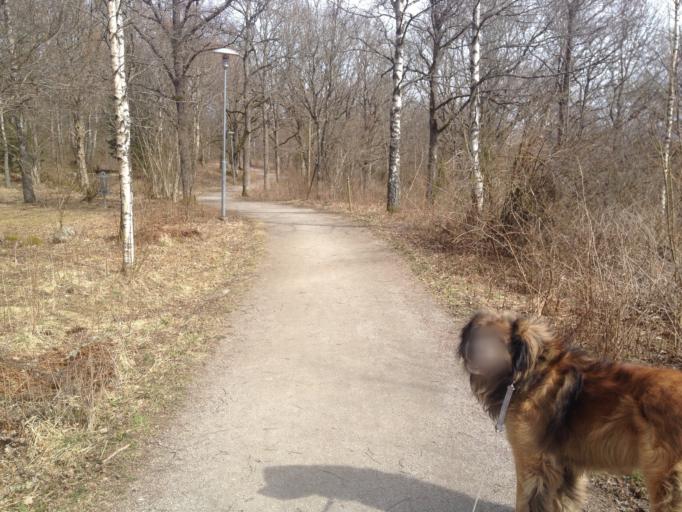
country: SE
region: Vaestra Goetaland
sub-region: Falkopings Kommun
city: Falkoeping
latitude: 58.1787
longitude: 13.5339
